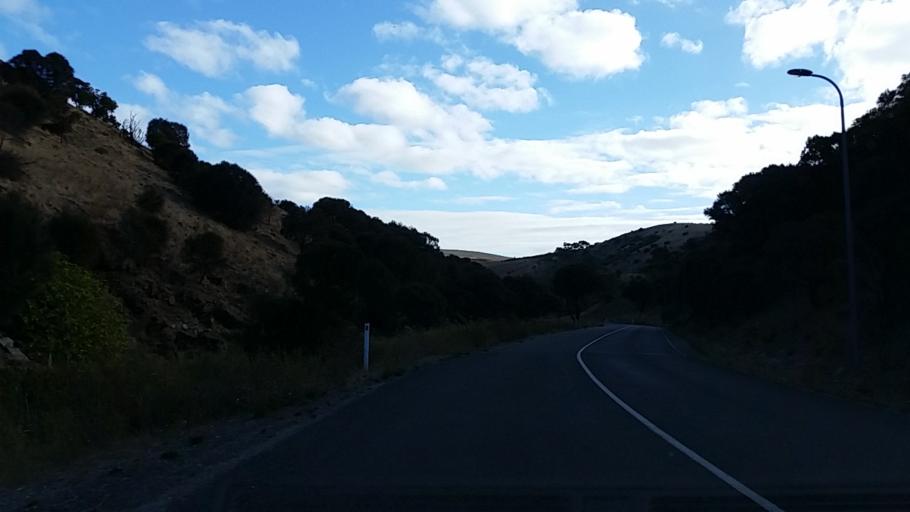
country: AU
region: South Australia
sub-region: Yankalilla
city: Normanville
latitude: -35.5023
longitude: 138.2478
